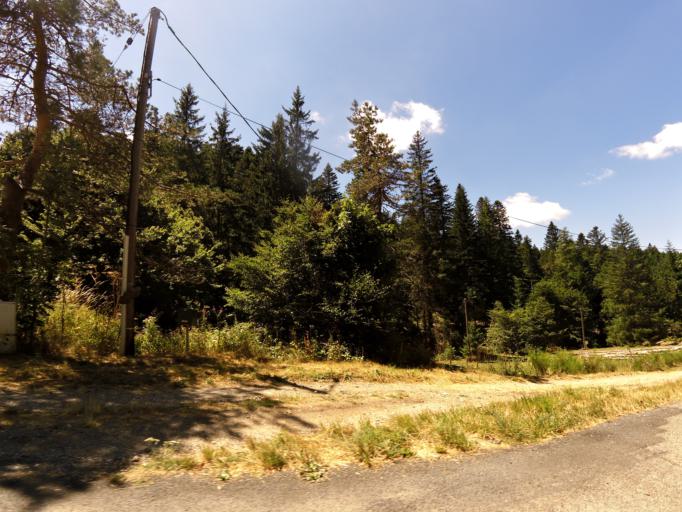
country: FR
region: Languedoc-Roussillon
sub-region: Departement de la Lozere
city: Meyrueis
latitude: 44.1034
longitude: 3.5007
